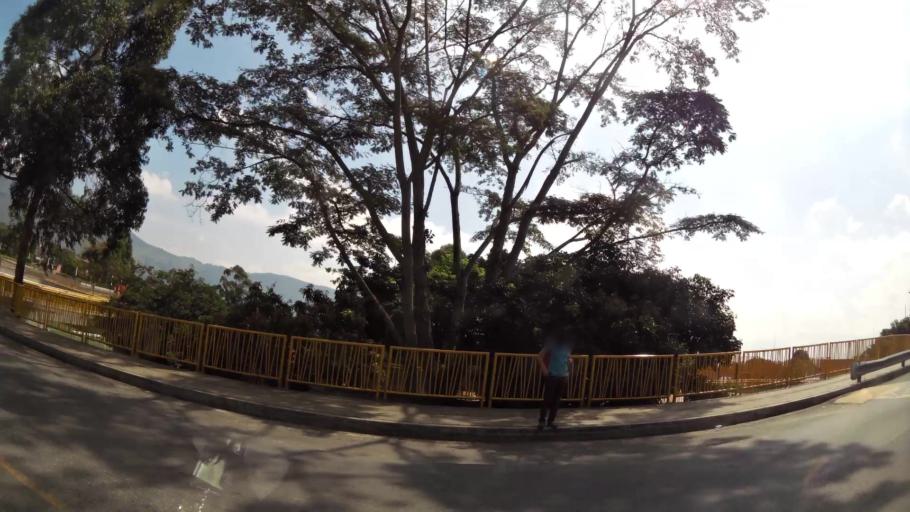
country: CO
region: Antioquia
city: La Estrella
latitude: 6.1771
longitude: -75.6541
